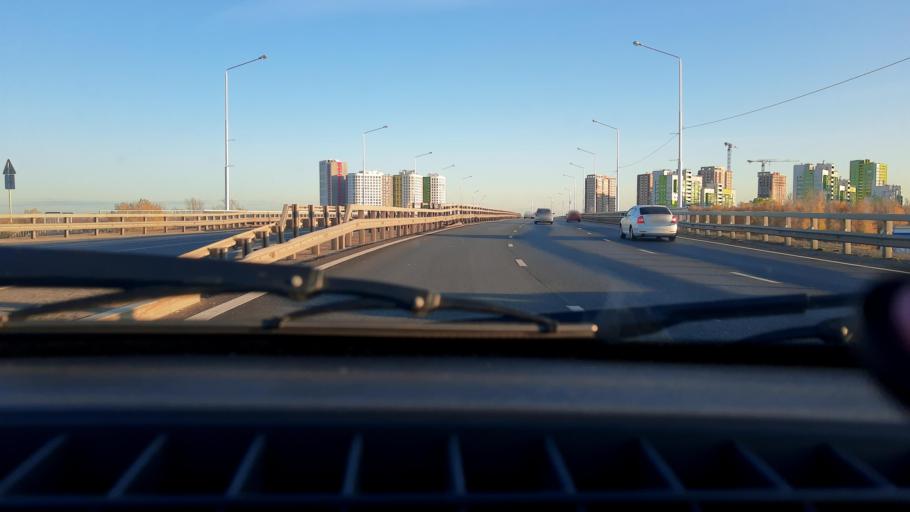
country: RU
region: Bashkortostan
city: Mikhaylovka
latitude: 54.7057
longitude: 55.8569
